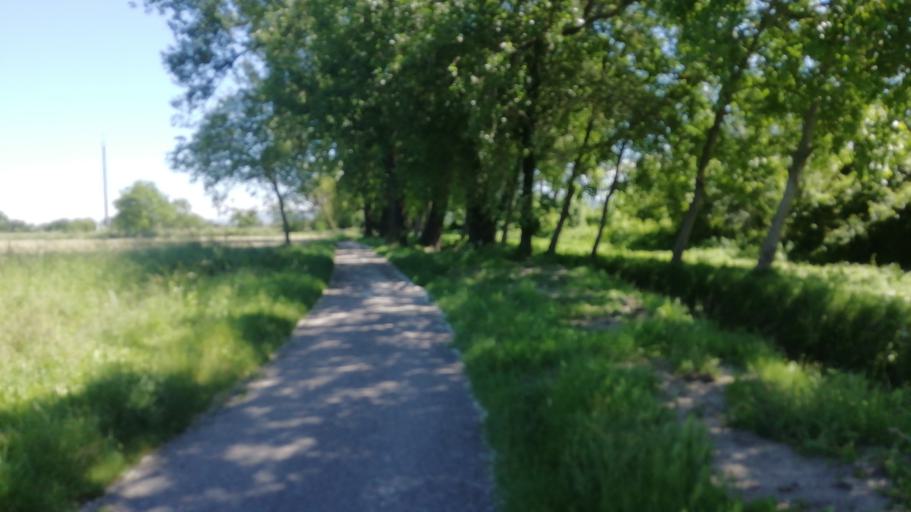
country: IT
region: Emilia-Romagna
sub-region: Provincia di Piacenza
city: Borgonovo Valtidone
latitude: 45.0055
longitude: 9.4485
